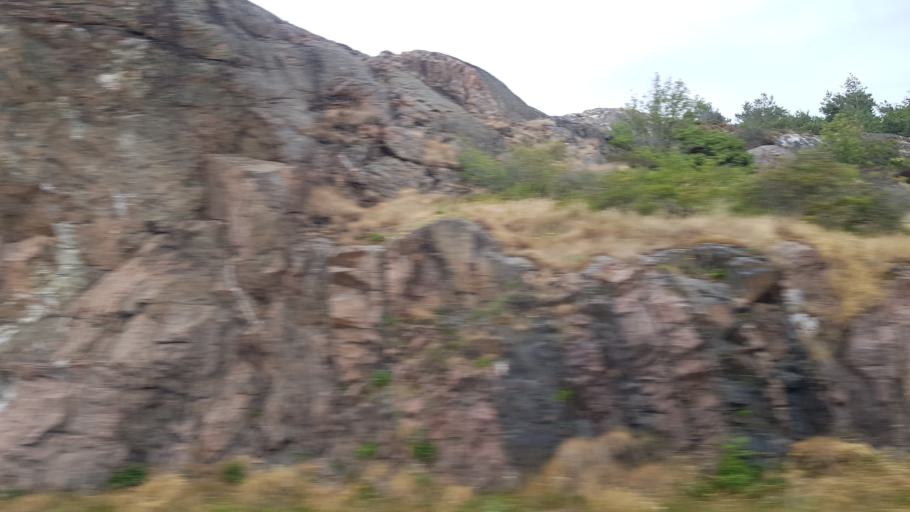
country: SE
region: Vaestra Goetaland
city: Ronnang
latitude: 57.9616
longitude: 11.5782
